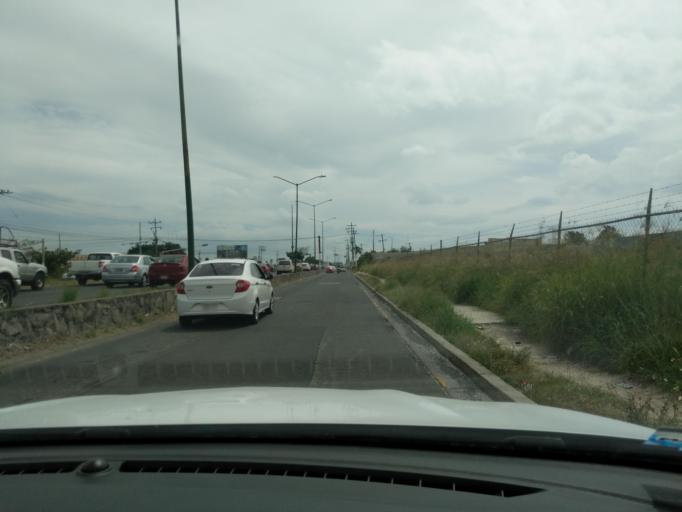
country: MX
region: Jalisco
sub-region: Zapopan
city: Puerta del Llano
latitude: 20.7835
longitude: -103.4658
